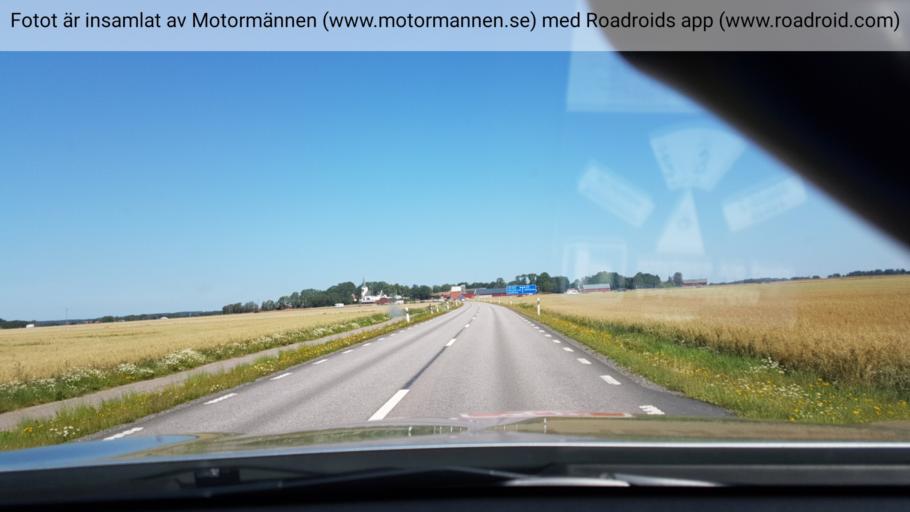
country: SE
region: Vaestra Goetaland
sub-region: Vara Kommun
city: Vara
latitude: 58.2901
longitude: 12.9609
